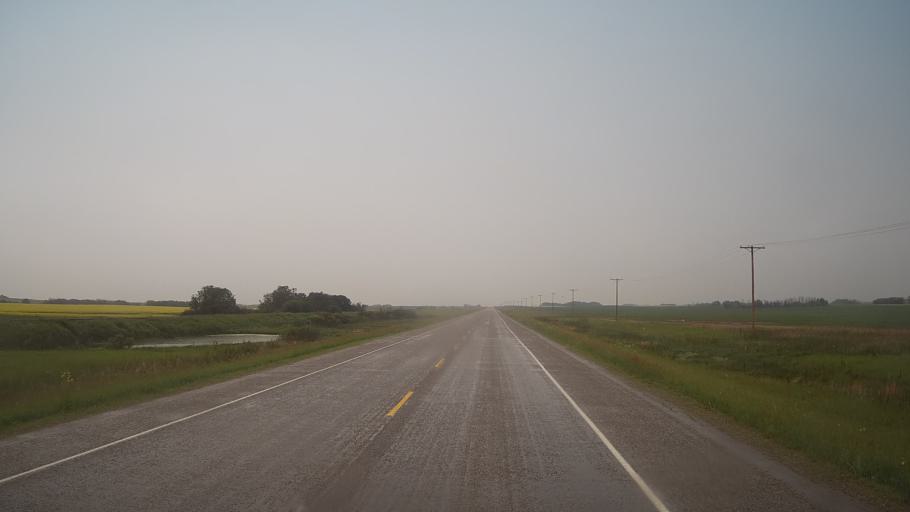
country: CA
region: Saskatchewan
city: Biggar
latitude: 52.1530
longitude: -108.2428
